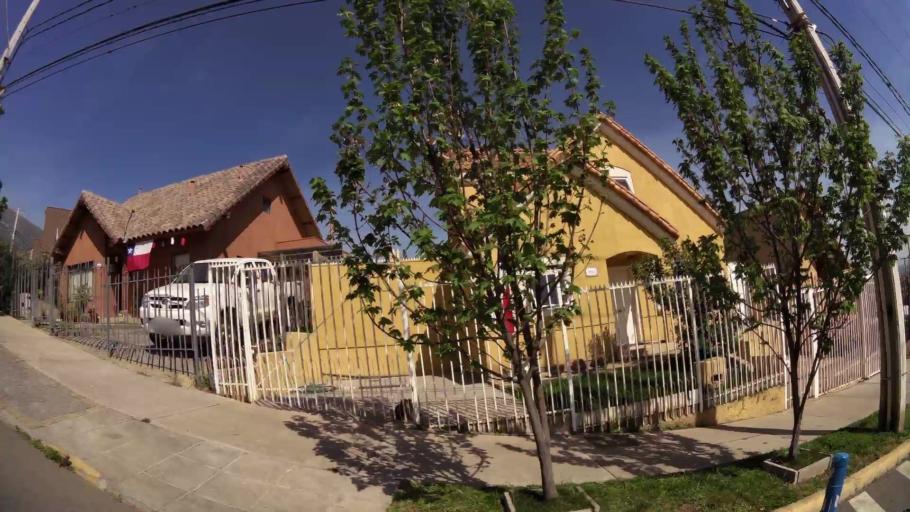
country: CL
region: Santiago Metropolitan
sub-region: Provincia de Santiago
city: Villa Presidente Frei, Nunoa, Santiago, Chile
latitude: -33.5347
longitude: -70.5427
